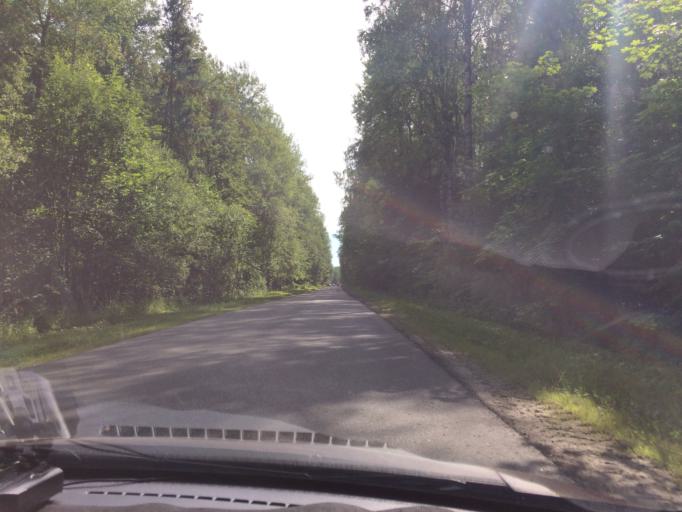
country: RU
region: Mariy-El
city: Surok
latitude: 56.5710
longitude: 48.1489
